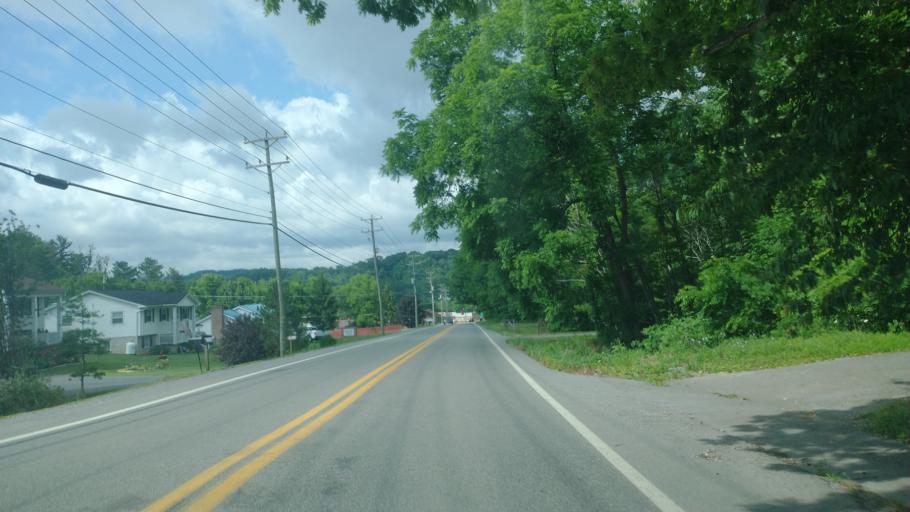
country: US
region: West Virginia
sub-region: Mercer County
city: Princeton
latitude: 37.3477
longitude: -81.1544
